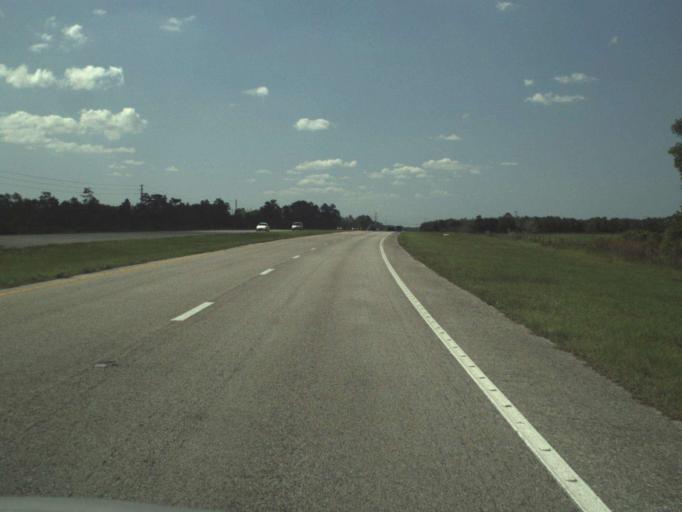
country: US
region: Florida
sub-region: Orange County
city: Wedgefield
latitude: 28.4912
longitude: -81.0413
